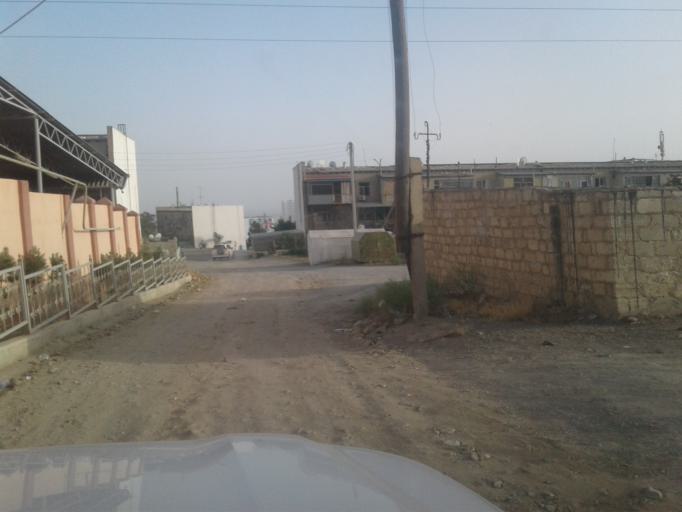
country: TM
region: Balkan
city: Turkmenbasy
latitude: 40.0066
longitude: 52.9651
